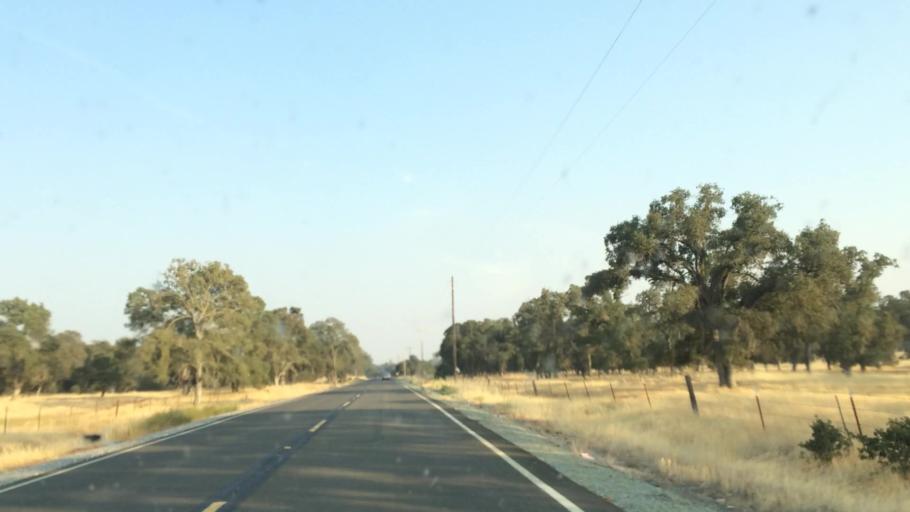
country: US
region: California
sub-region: Amador County
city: Ione
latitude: 38.3904
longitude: -120.9954
